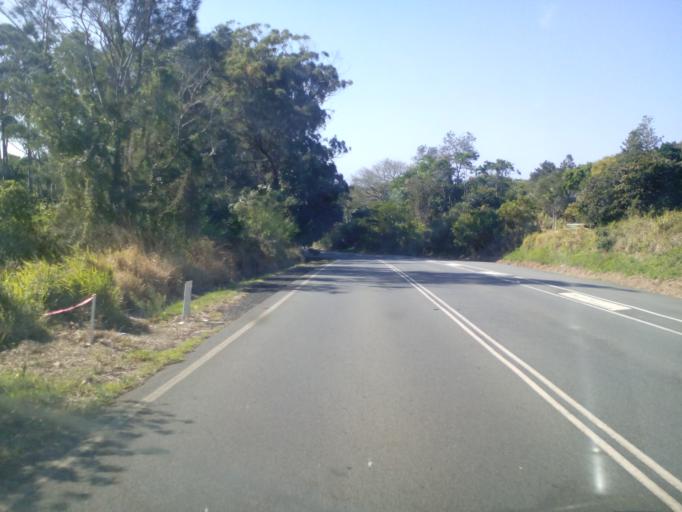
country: AU
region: New South Wales
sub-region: Tweed
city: Kingscliff
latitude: -28.2622
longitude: 153.5705
